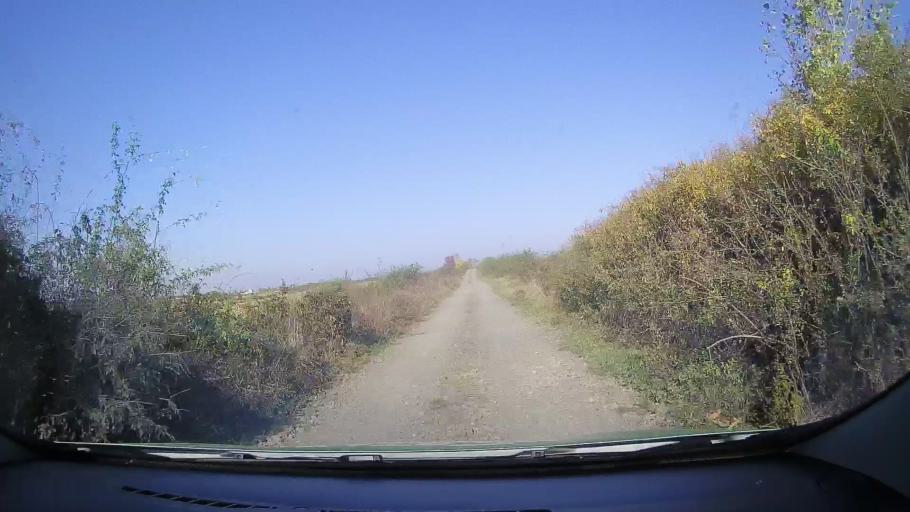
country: RO
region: Satu Mare
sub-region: Comuna Sauca
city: Sauca
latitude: 47.4830
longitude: 22.4652
